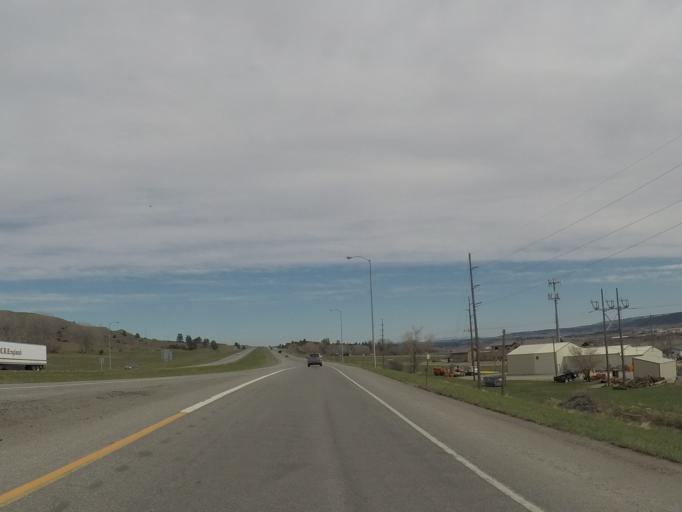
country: US
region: Montana
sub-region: Stillwater County
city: Columbus
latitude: 45.6453
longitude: -109.2451
